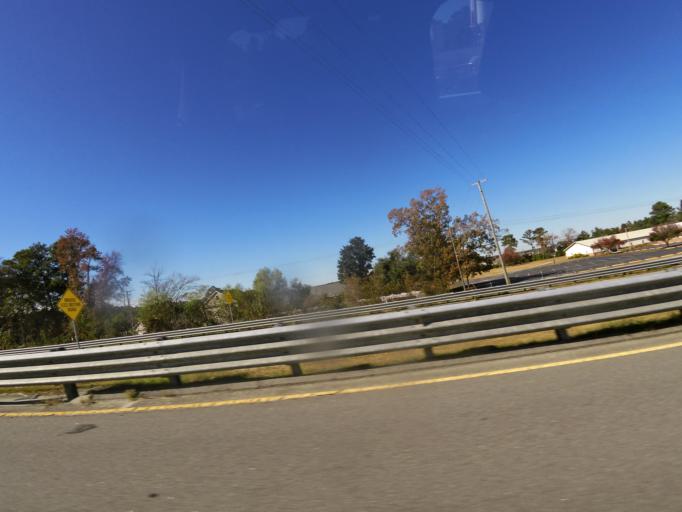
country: US
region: Georgia
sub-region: Bryan County
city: Richmond Hill
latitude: 31.9389
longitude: -81.3188
